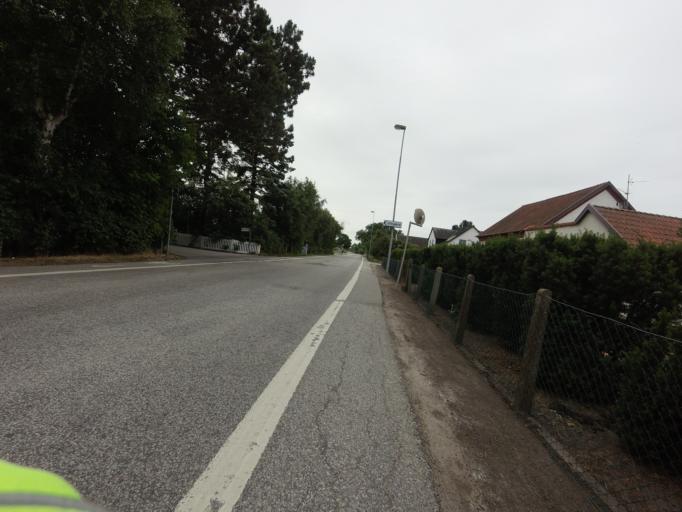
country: SE
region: Skane
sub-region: Malmo
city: Bunkeflostrand
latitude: 55.5359
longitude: 12.9215
